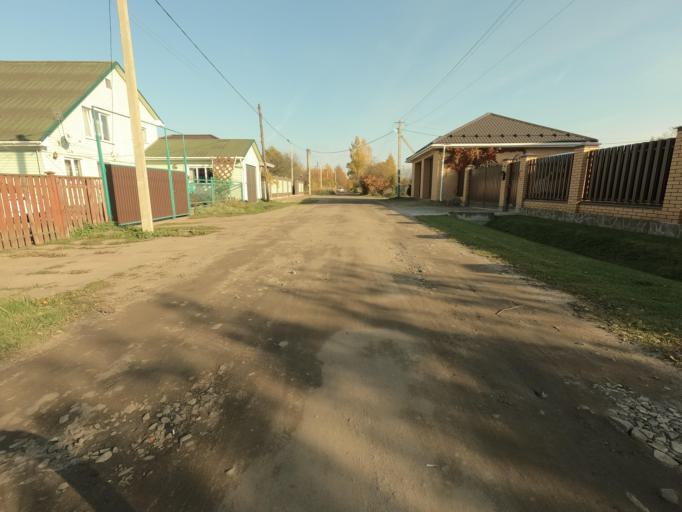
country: RU
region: Leningrad
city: Mga
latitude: 59.7526
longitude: 31.0642
